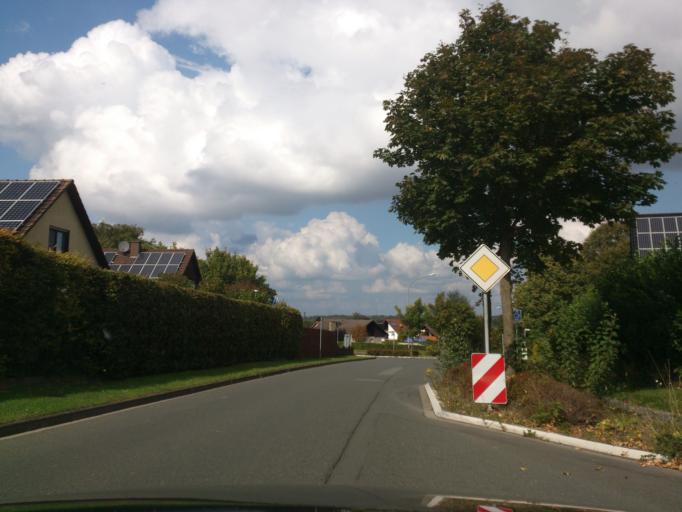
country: DE
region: North Rhine-Westphalia
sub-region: Regierungsbezirk Detmold
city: Paderborn
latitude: 51.6525
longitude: 8.7199
